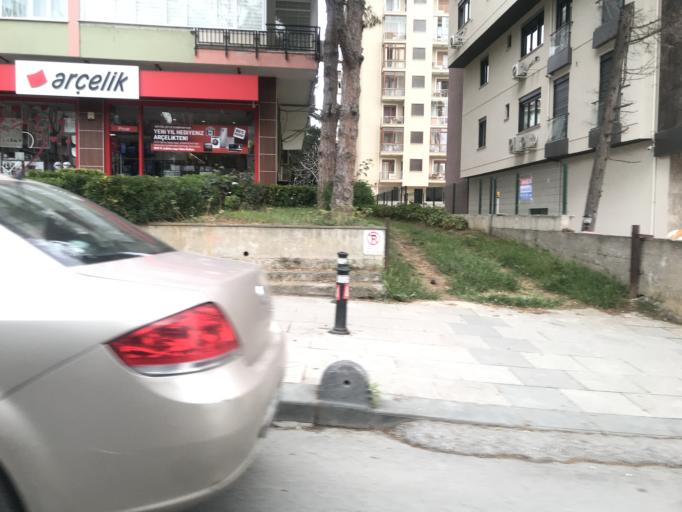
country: TR
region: Istanbul
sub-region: Atasehir
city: Atasehir
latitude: 40.9622
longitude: 29.0916
